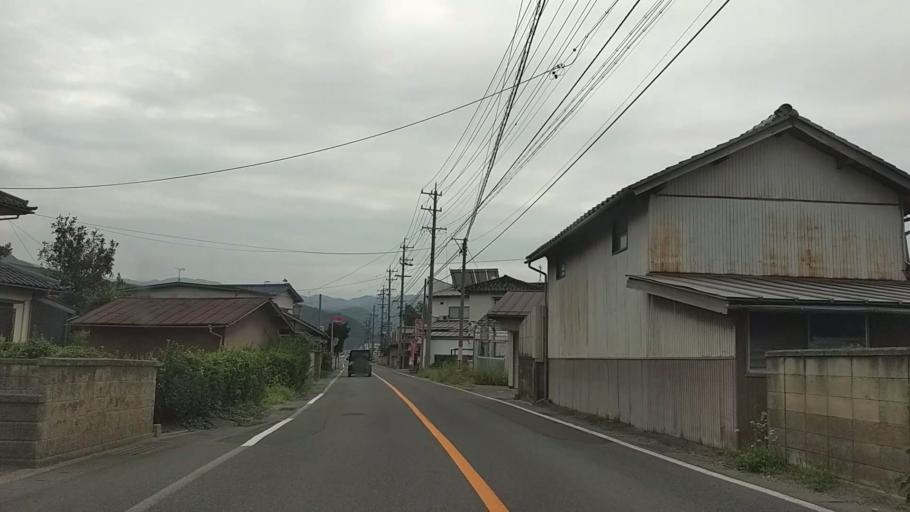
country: JP
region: Nagano
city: Nagano-shi
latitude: 36.5876
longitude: 138.1982
